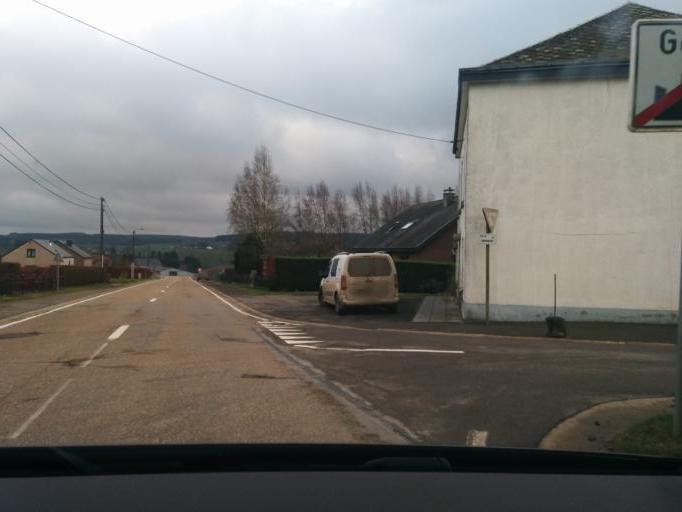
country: BE
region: Wallonia
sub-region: Province du Luxembourg
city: Gouvy
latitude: 50.1883
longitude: 5.9634
